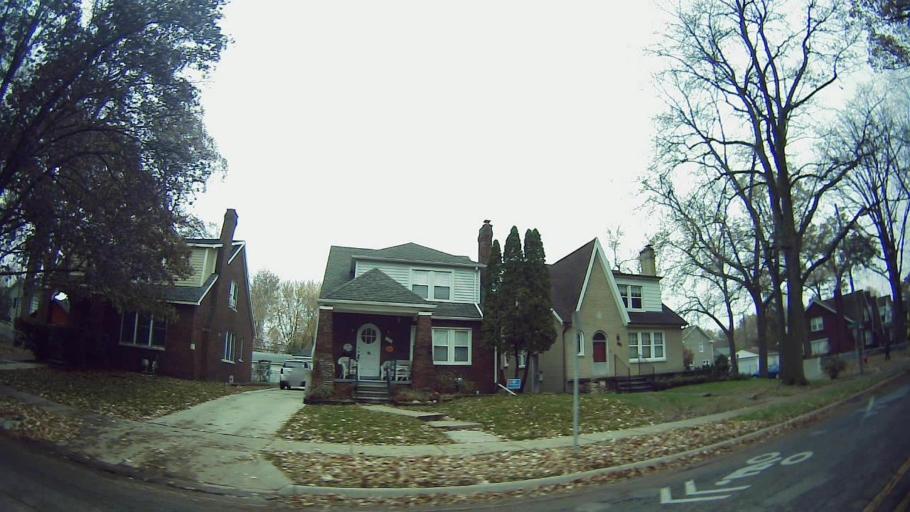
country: US
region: Michigan
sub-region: Oakland County
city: Royal Oak
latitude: 42.4980
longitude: -83.1343
